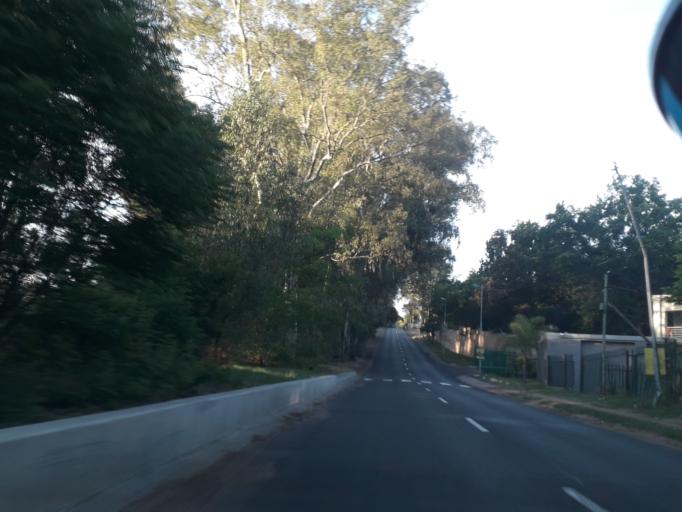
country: ZA
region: Gauteng
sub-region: City of Johannesburg Metropolitan Municipality
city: Diepsloot
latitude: -26.0574
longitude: 28.0037
